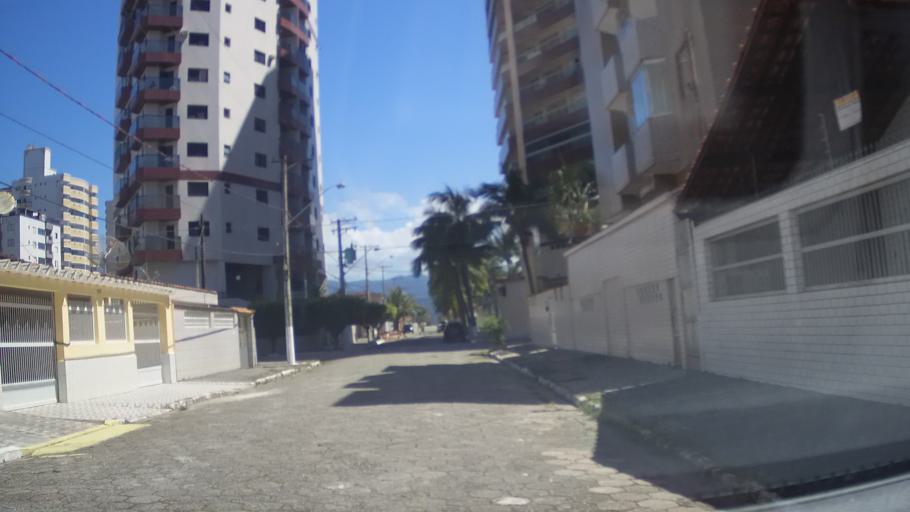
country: BR
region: Sao Paulo
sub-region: Praia Grande
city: Praia Grande
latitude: -24.0273
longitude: -46.4723
